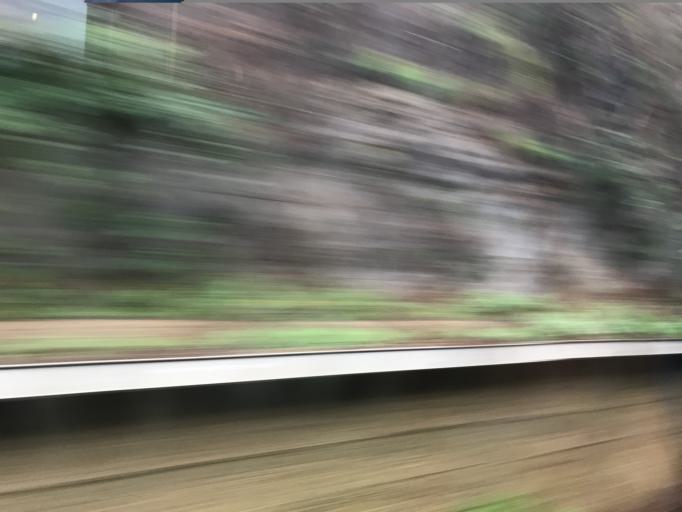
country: VA
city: Vatican City
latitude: 41.8493
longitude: 12.4554
